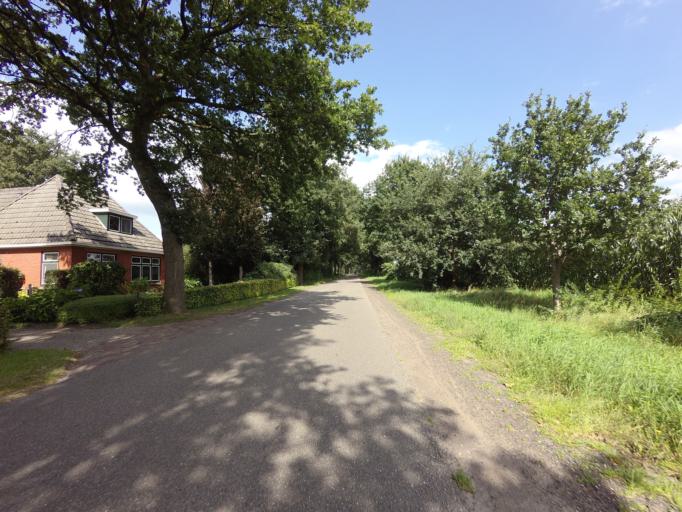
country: NL
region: Friesland
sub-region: Gemeente Heerenveen
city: Jubbega
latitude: 52.9875
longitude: 6.2245
